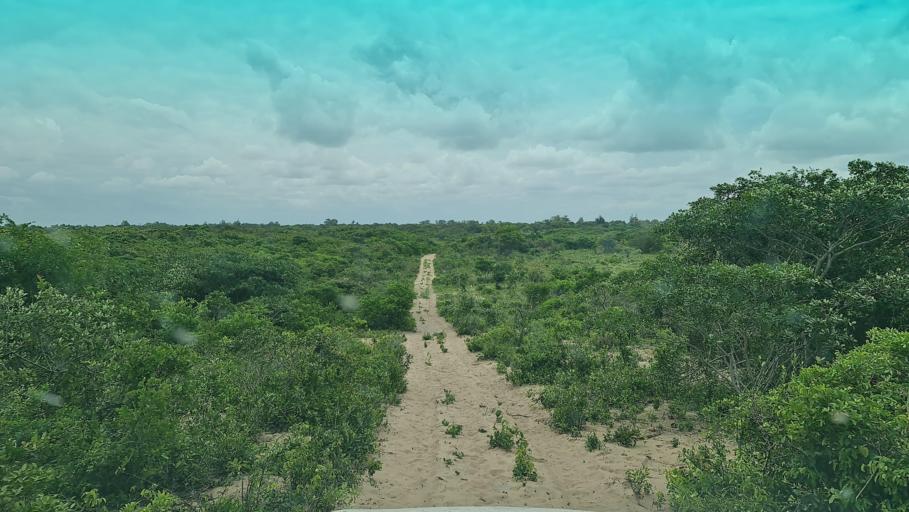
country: MZ
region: Maputo
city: Manhica
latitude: -25.6243
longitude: 32.7785
